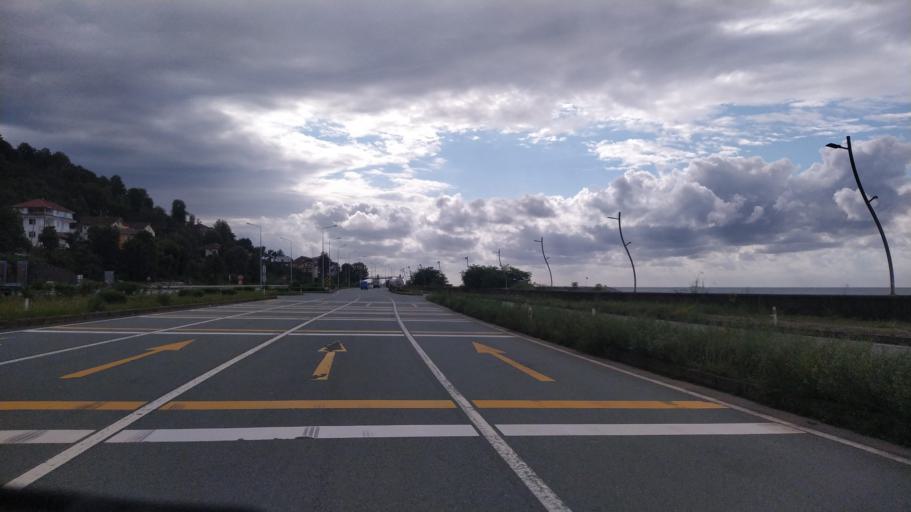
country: TR
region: Rize
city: Ardesen
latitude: 41.2105
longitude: 41.0423
